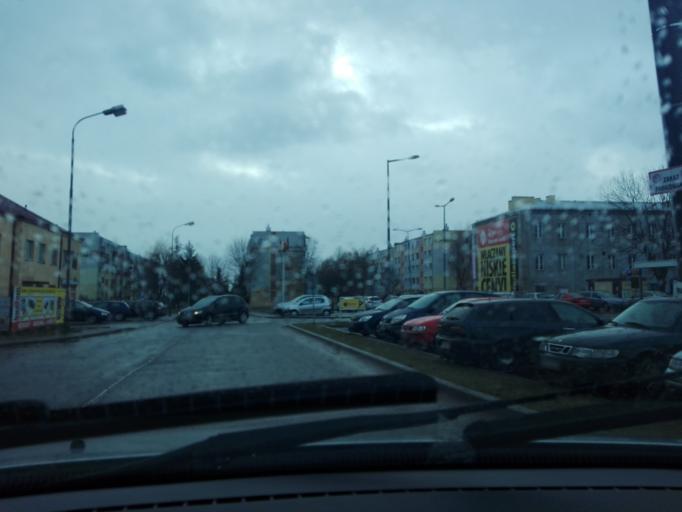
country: PL
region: Lodz Voivodeship
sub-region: Powiat kutnowski
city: Kutno
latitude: 52.2296
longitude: 19.3715
